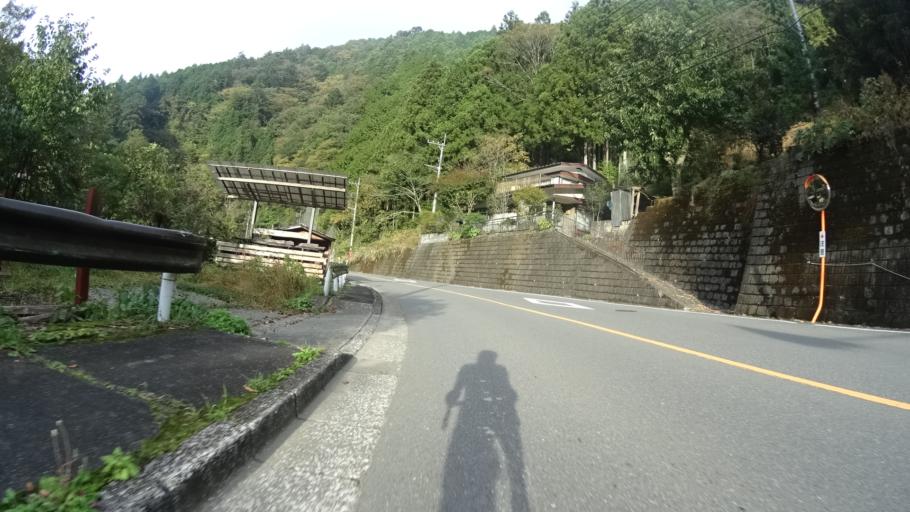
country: JP
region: Tokyo
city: Itsukaichi
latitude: 35.7029
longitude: 139.1373
